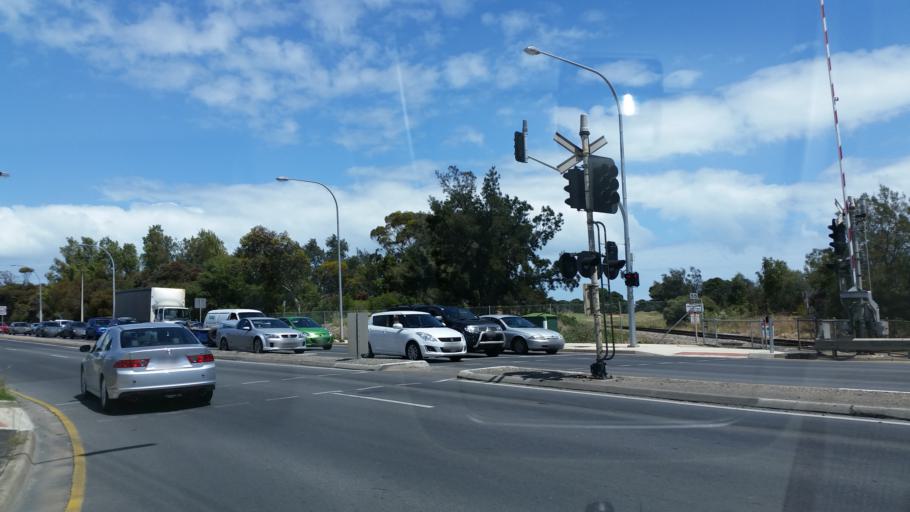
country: AU
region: South Australia
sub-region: Charles Sturt
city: Seaton
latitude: -34.8919
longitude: 138.5138
